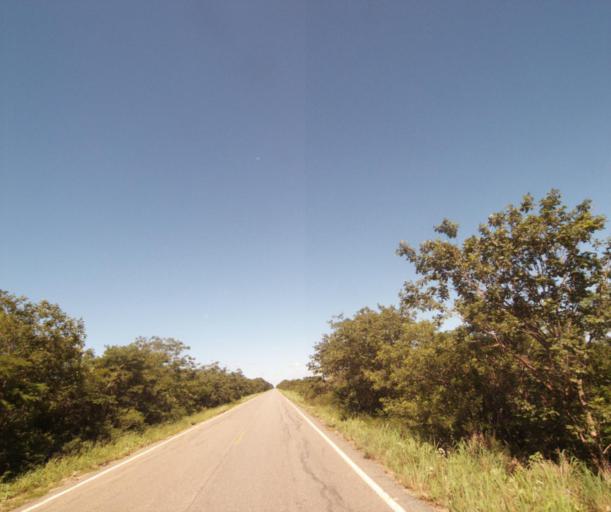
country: BR
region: Bahia
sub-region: Carinhanha
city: Carinhanha
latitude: -14.2830
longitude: -43.5648
